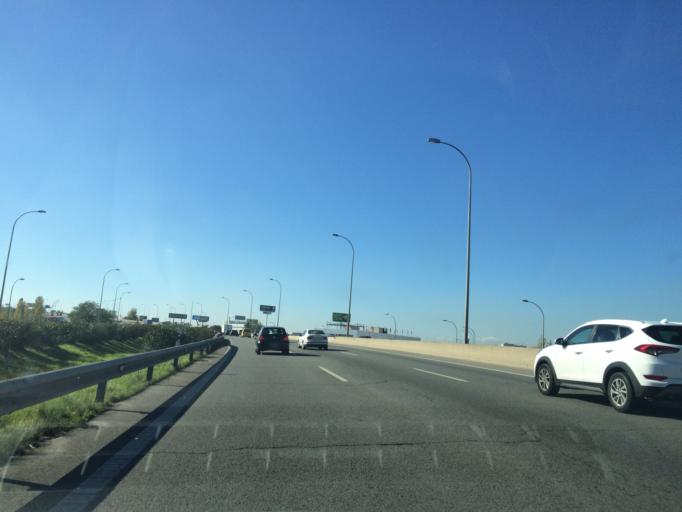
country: ES
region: Madrid
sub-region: Provincia de Madrid
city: Alcobendas
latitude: 40.5331
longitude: -3.6371
